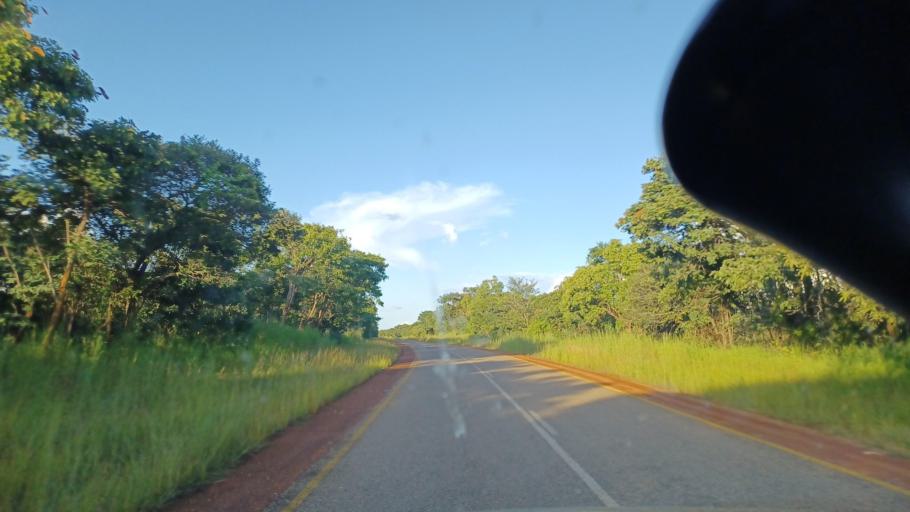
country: ZM
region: North-Western
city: Kalengwa
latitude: -13.1416
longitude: 25.0641
